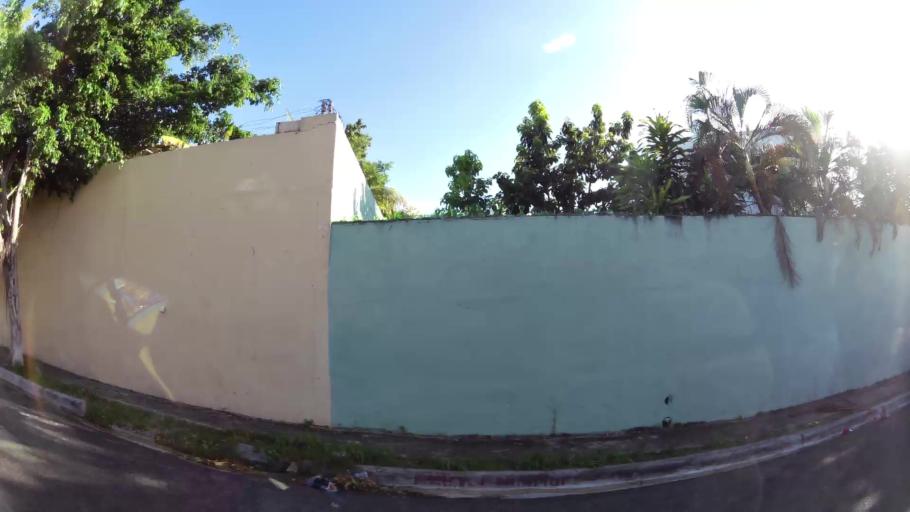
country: DO
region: Nacional
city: Santo Domingo
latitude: 18.4962
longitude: -69.9691
